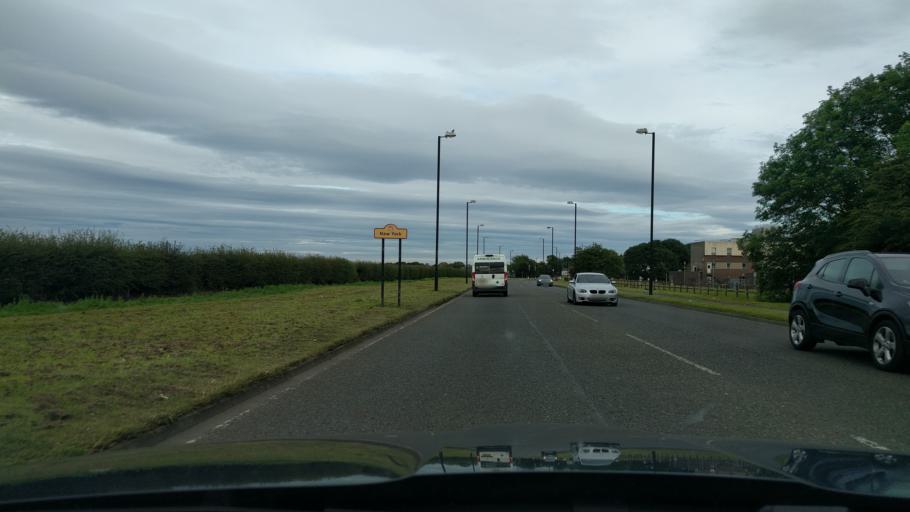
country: GB
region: England
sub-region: Borough of North Tyneside
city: Shiremoor
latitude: 55.0269
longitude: -1.5021
